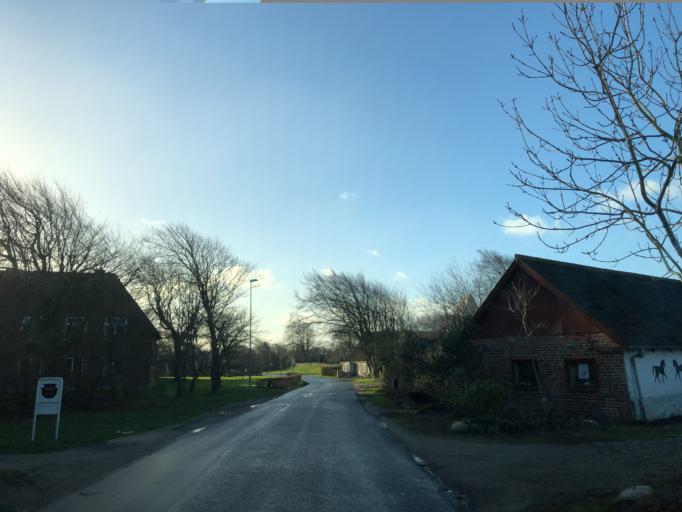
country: DK
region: Central Jutland
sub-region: Holstebro Kommune
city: Ulfborg
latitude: 56.2082
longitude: 8.2572
